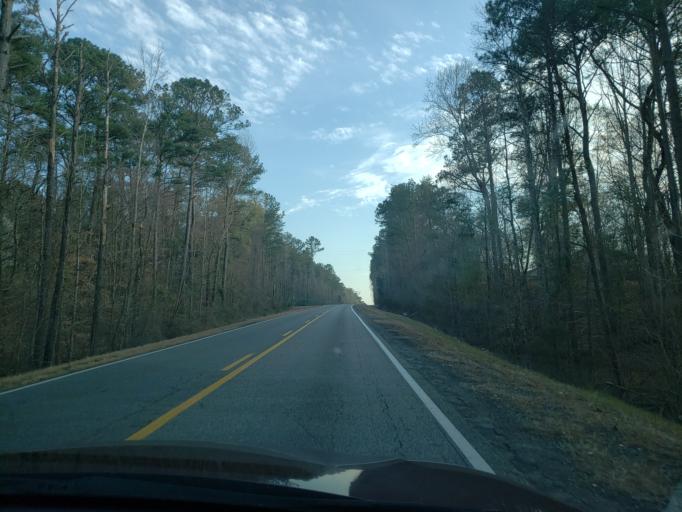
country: US
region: Alabama
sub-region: Hale County
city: Greensboro
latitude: 32.7487
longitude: -87.5851
